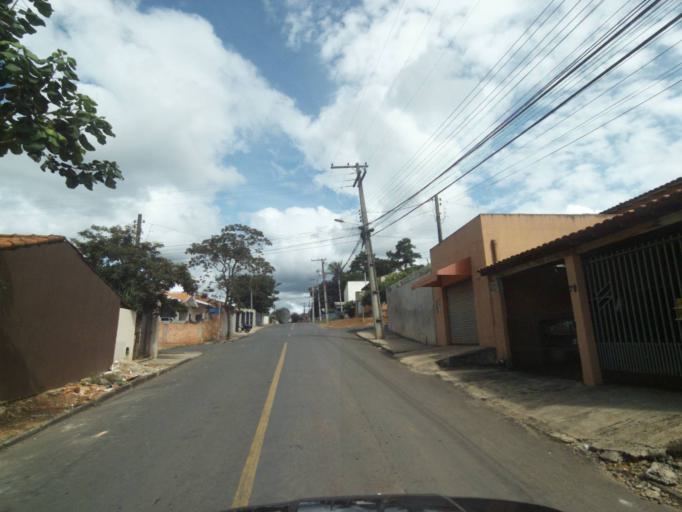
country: BR
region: Parana
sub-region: Telemaco Borba
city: Telemaco Borba
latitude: -24.3157
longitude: -50.6312
